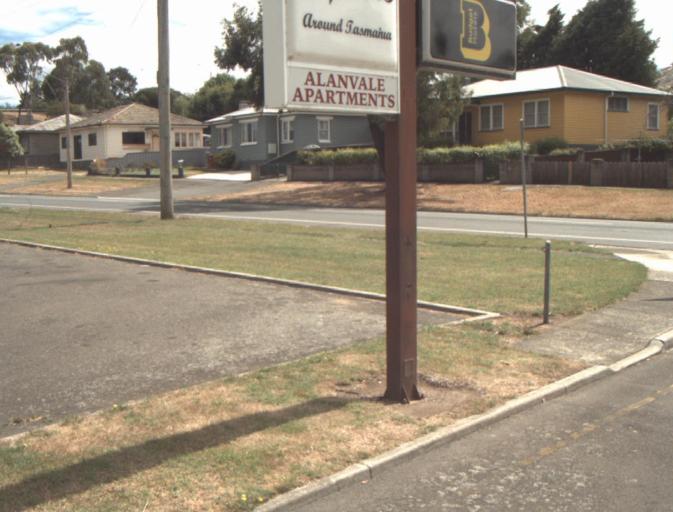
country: AU
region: Tasmania
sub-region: Launceston
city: Newnham
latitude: -41.3957
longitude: 147.1257
